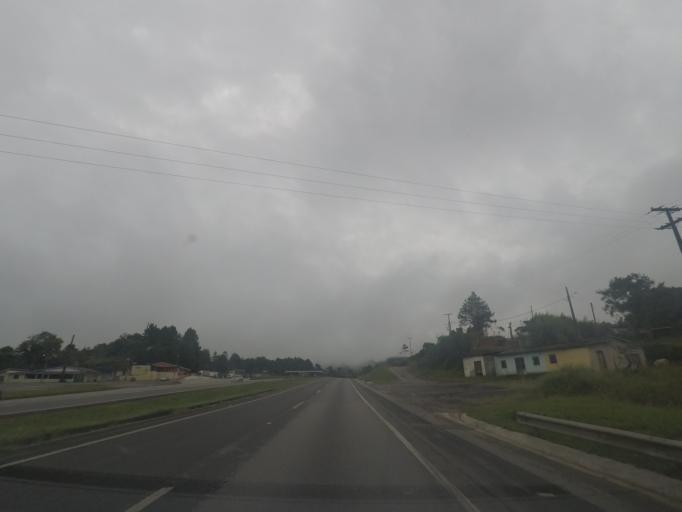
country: BR
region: Parana
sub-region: Antonina
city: Antonina
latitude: -25.0839
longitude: -48.6006
